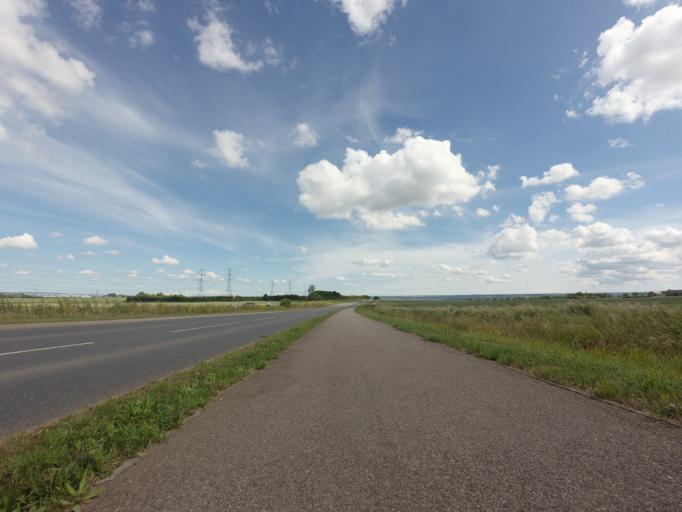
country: GB
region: England
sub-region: Kent
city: Hoo
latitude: 51.4338
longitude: 0.5703
